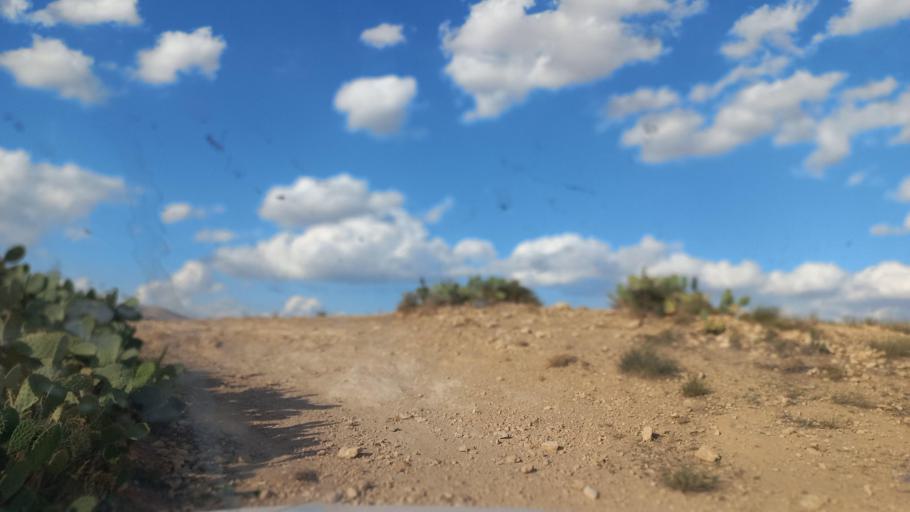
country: TN
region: Al Qasrayn
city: Sbiba
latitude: 35.3905
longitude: 9.0432
